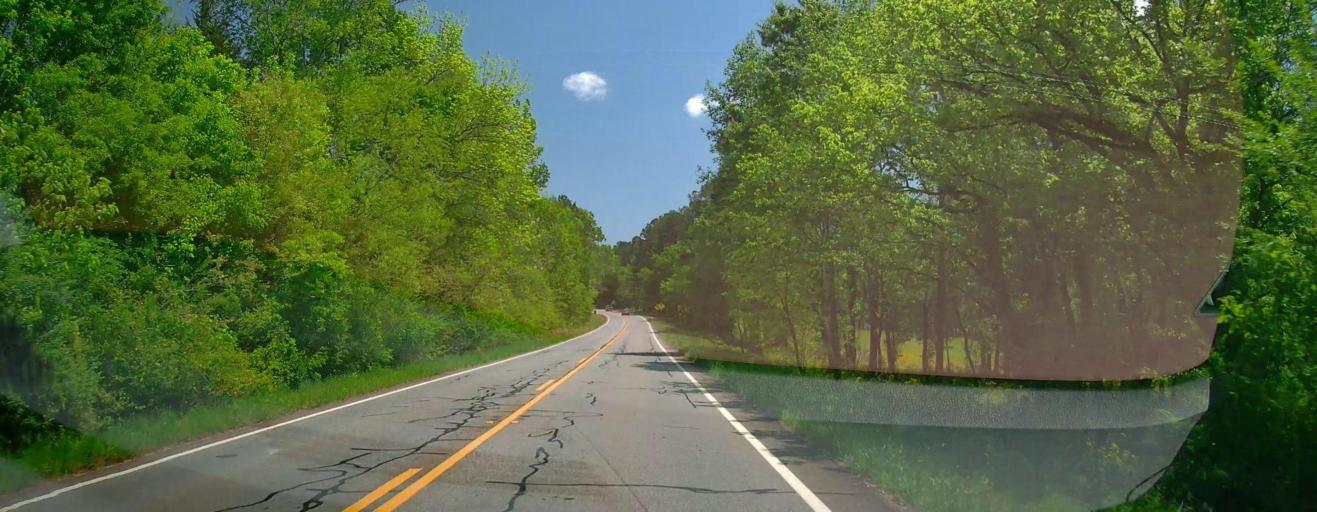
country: US
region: Georgia
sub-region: Jasper County
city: Monticello
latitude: 33.3139
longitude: -83.7104
